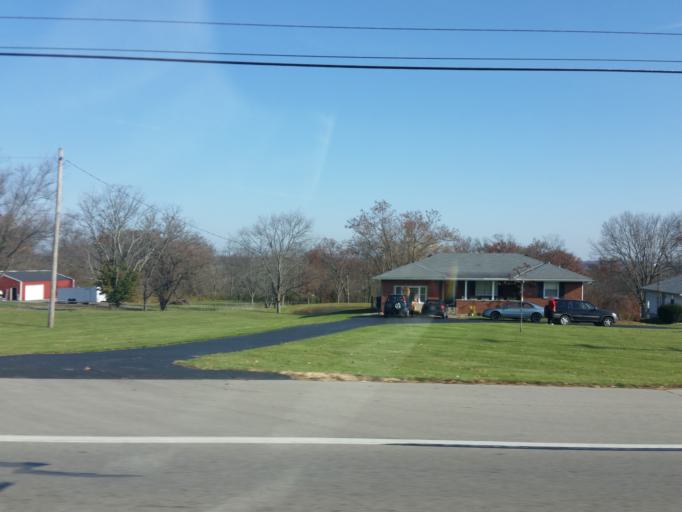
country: US
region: Ohio
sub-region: Butler County
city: Ross
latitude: 39.4145
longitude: -84.6743
